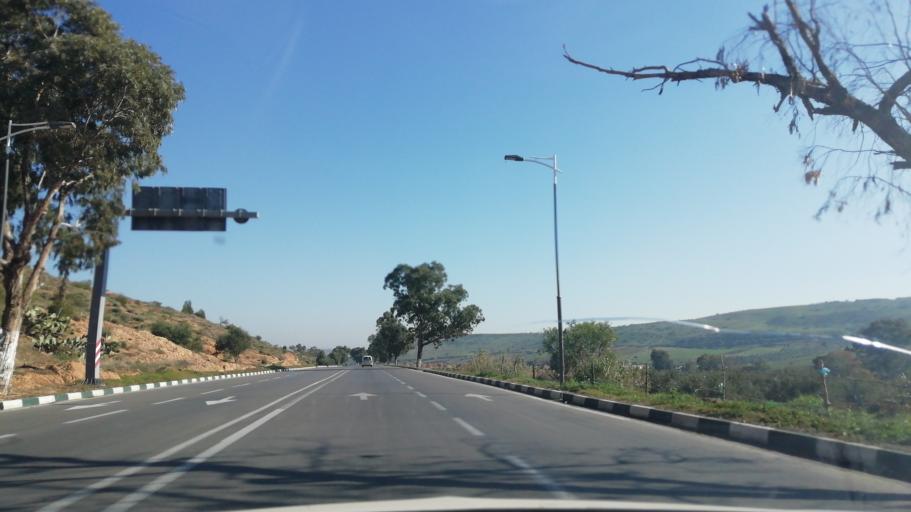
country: DZ
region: Tlemcen
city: Remchi
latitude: 35.0515
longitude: -1.5359
